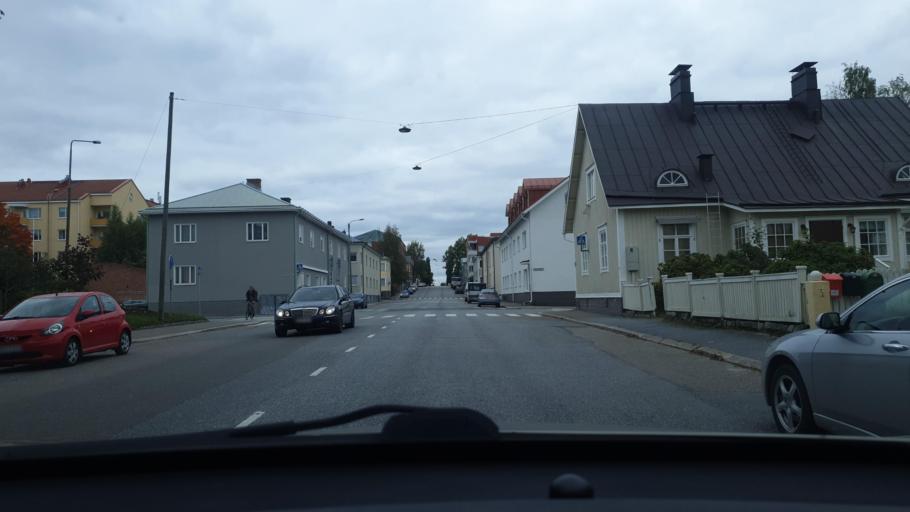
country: FI
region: Ostrobothnia
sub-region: Vaasa
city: Vaasa
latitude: 63.0882
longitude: 21.6291
